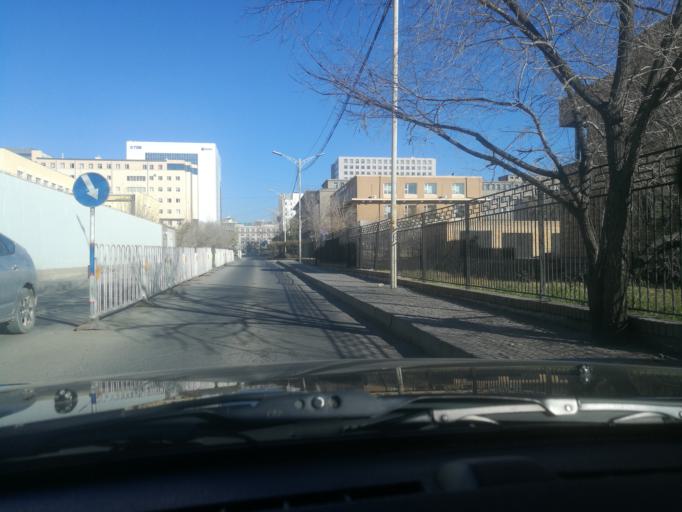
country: MN
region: Ulaanbaatar
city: Ulaanbaatar
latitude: 47.9145
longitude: 106.9238
